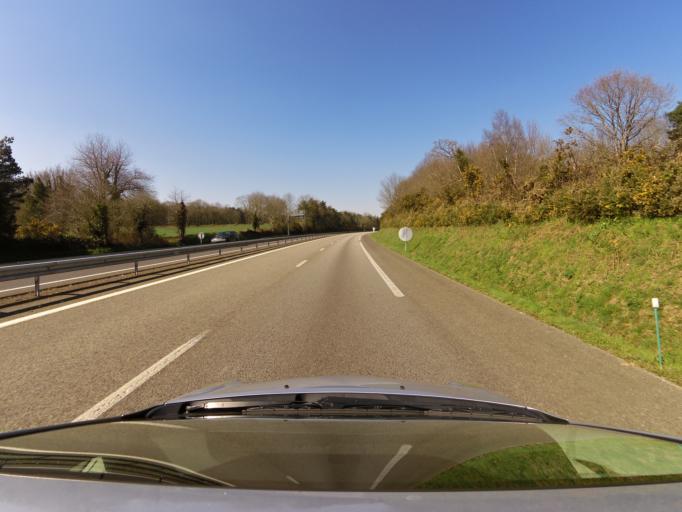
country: FR
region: Brittany
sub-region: Departement du Morbihan
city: Guillac
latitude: 47.9366
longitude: -2.4832
